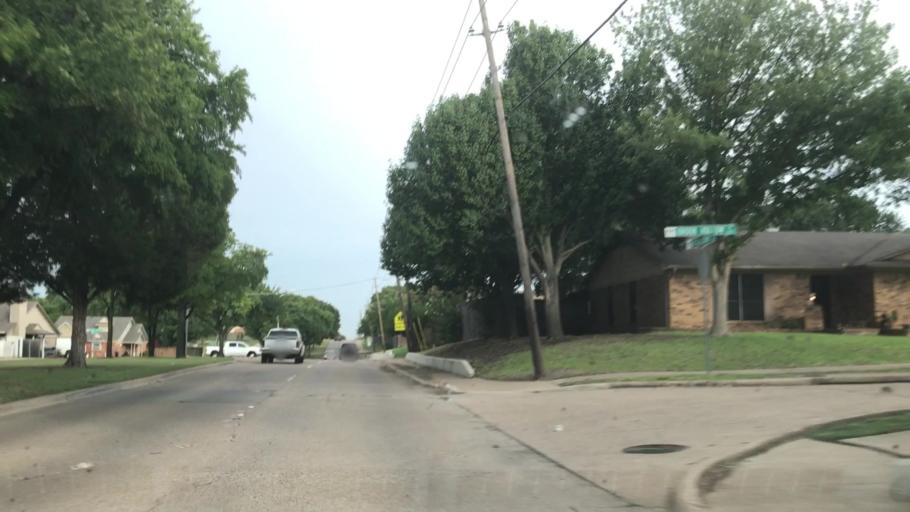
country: US
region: Texas
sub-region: Dallas County
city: Garland
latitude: 32.8383
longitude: -96.6393
